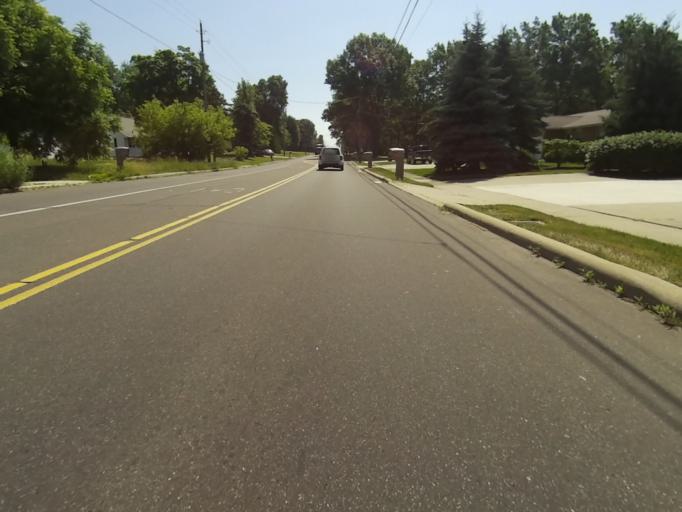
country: US
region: Ohio
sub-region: Summit County
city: Stow
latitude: 41.1667
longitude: -81.4269
